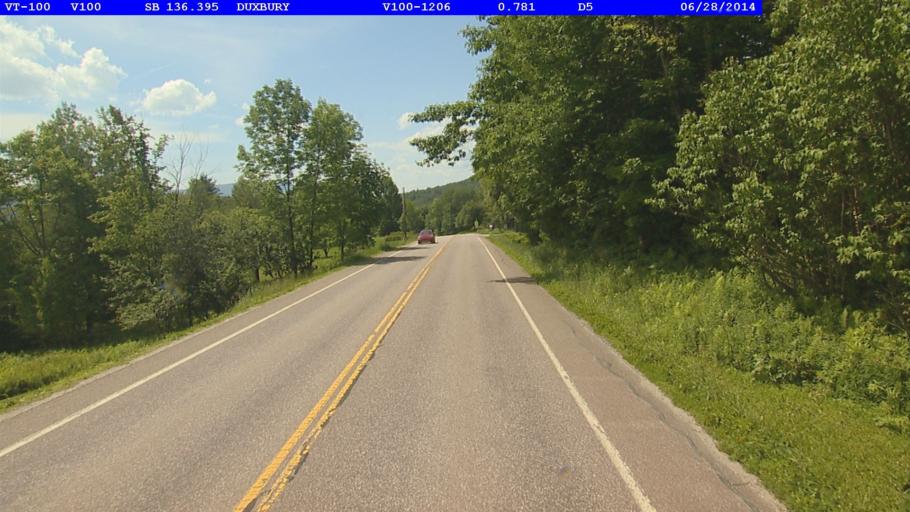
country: US
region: Vermont
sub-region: Washington County
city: Waterbury
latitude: 44.2577
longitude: -72.7884
